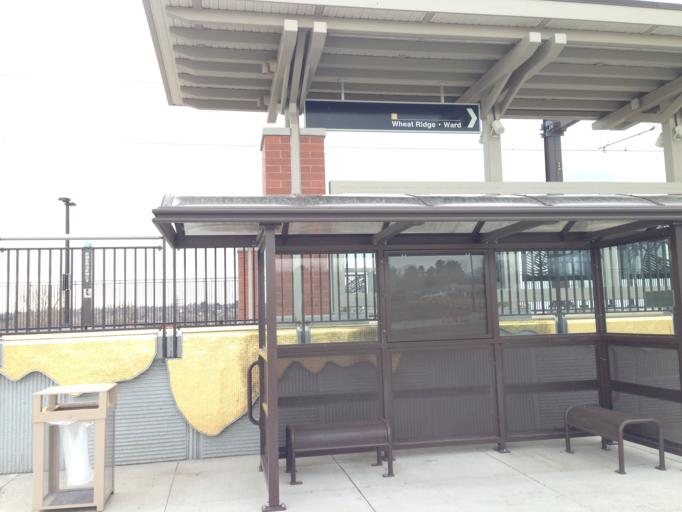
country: US
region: Colorado
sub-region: Adams County
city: Berkley
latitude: 39.8038
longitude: -105.0493
